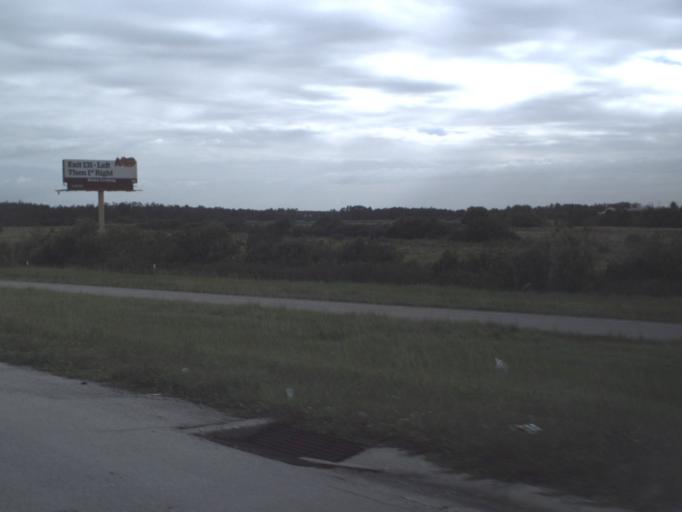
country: US
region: Florida
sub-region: Lee County
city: Fort Myers
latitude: 26.6102
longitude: -81.8026
